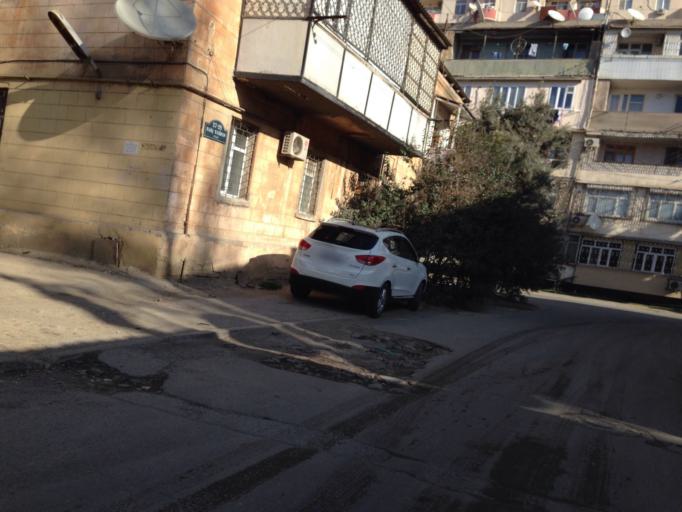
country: AZ
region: Baki
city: Baku
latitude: 40.4010
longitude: 49.8752
